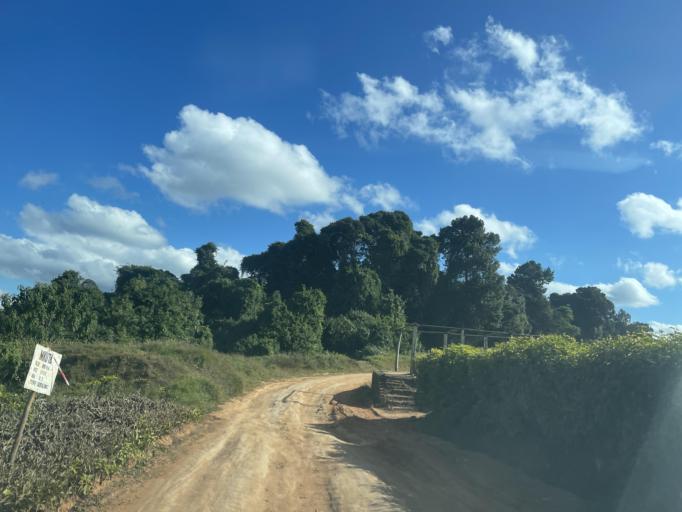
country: TZ
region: Iringa
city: Makungu
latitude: -8.4641
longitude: 35.4320
